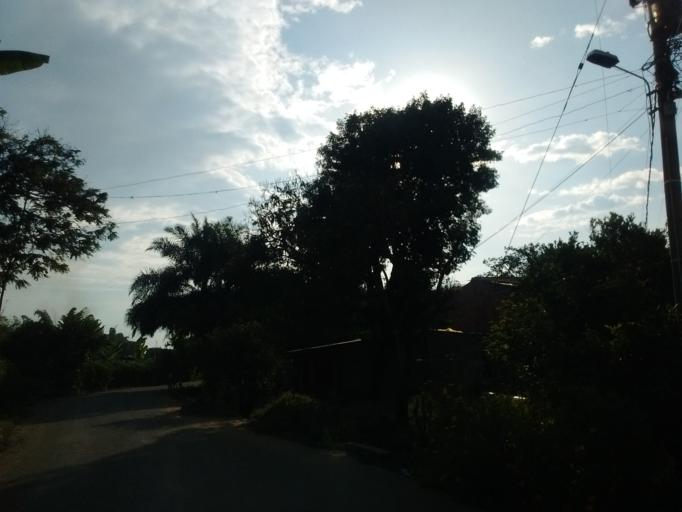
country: CO
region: Cauca
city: Puerto Tejada
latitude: 3.2010
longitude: -76.4422
